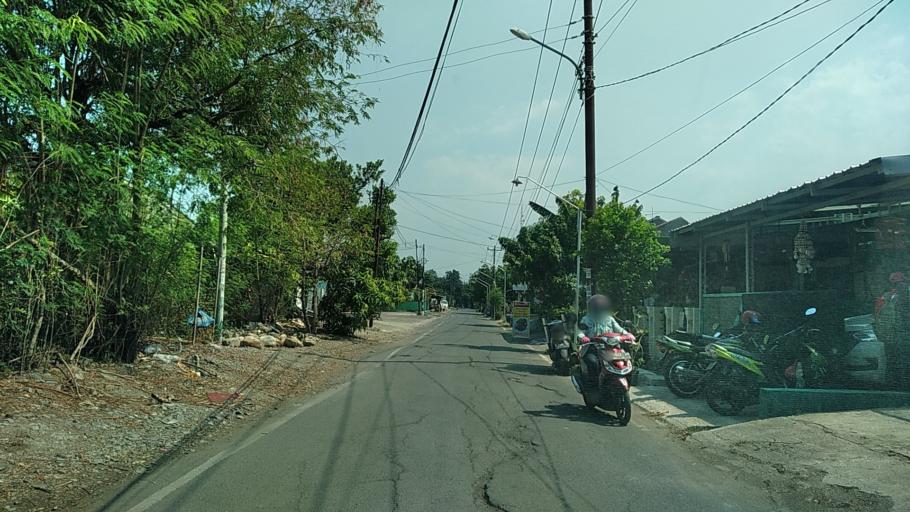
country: ID
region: Central Java
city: Mranggen
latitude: -7.0453
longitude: 110.4814
